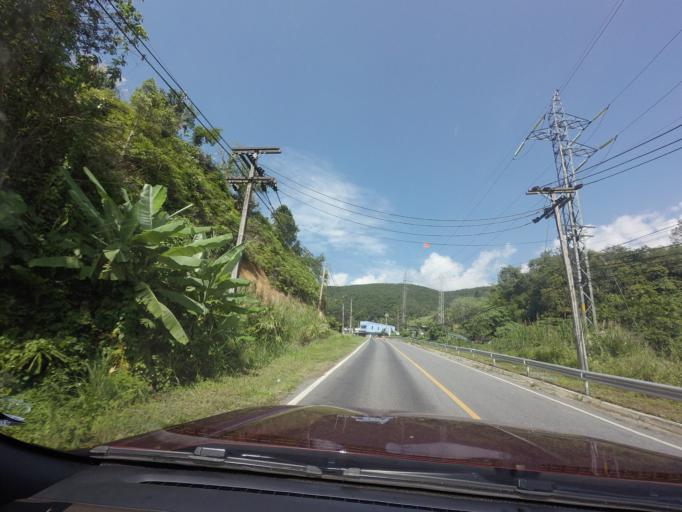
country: TH
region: Yala
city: Betong
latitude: 5.9022
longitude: 101.1459
